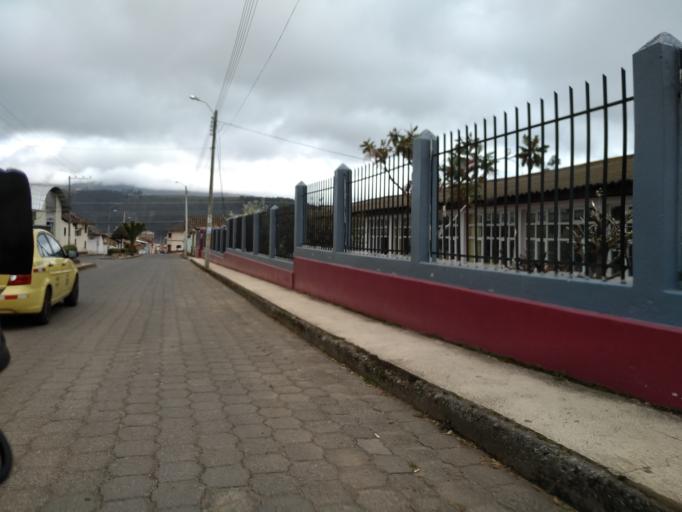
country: EC
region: Carchi
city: El Angel
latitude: 0.6249
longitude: -77.9370
